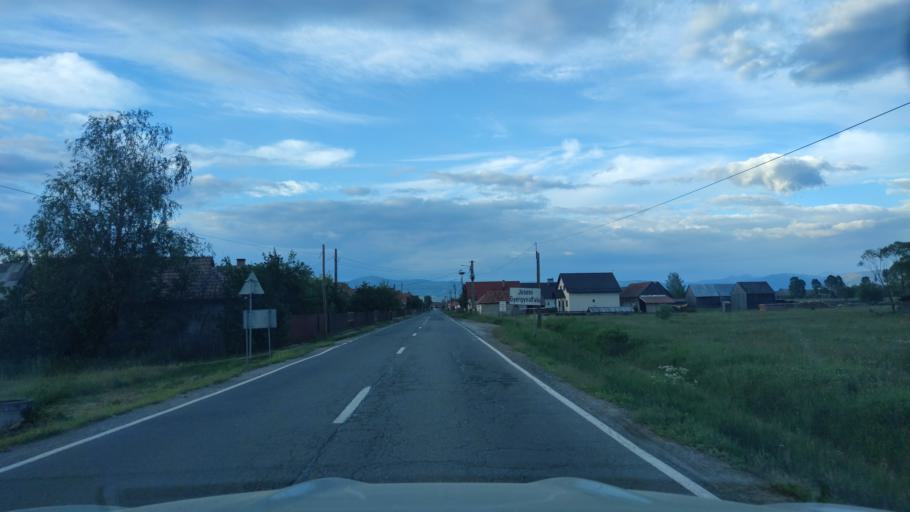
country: RO
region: Harghita
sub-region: Comuna Joseni
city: Joseni
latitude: 46.6990
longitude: 25.4850
